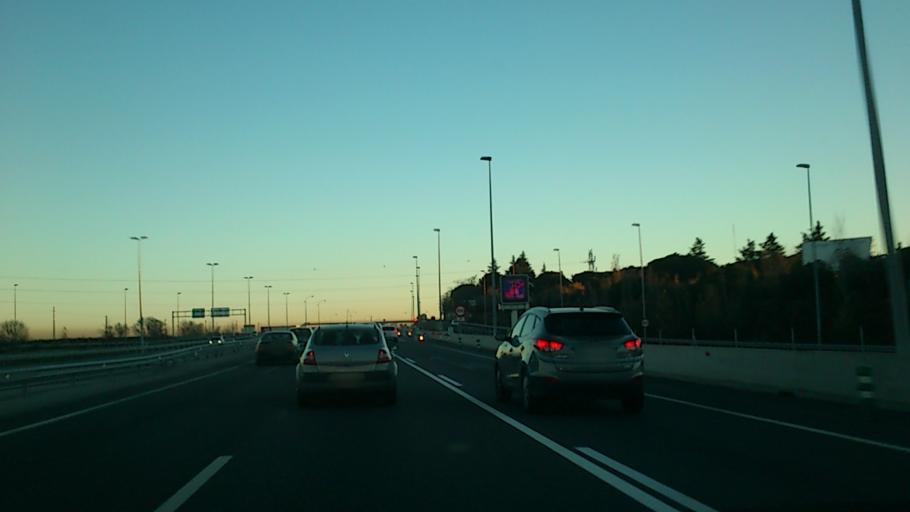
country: ES
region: Madrid
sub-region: Provincia de Madrid
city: Las Rozas de Madrid
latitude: 40.5080
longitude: -3.8779
